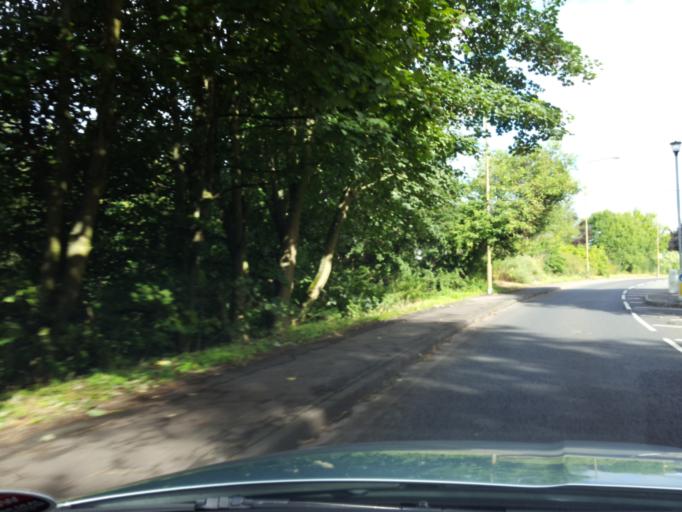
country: GB
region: Scotland
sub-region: West Lothian
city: Linlithgow
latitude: 55.9794
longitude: -3.6129
